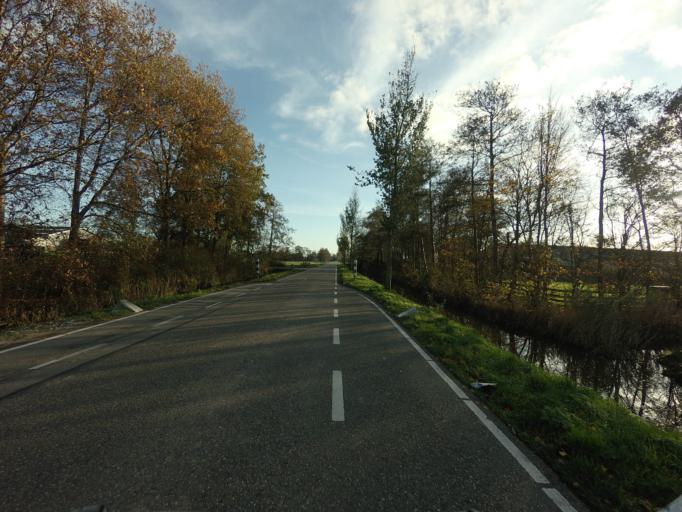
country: NL
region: South Holland
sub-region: Gemeente Nieuwkoop
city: Nieuwkoop
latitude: 52.1792
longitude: 4.8110
